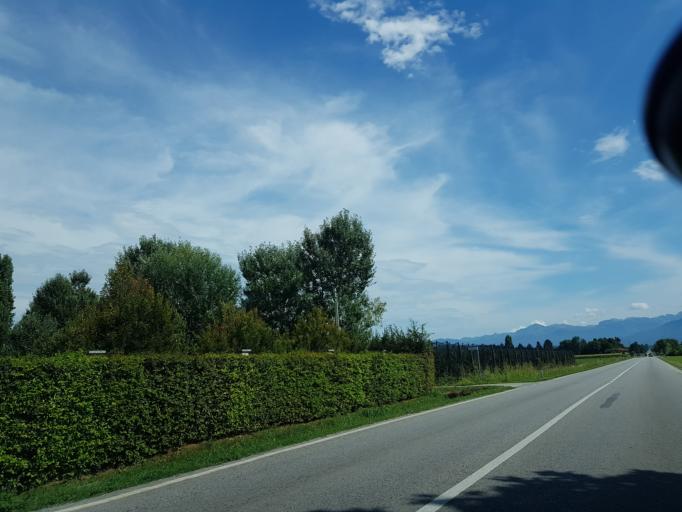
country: IT
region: Piedmont
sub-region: Provincia di Cuneo
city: Roata Rossi
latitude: 44.4679
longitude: 7.5136
